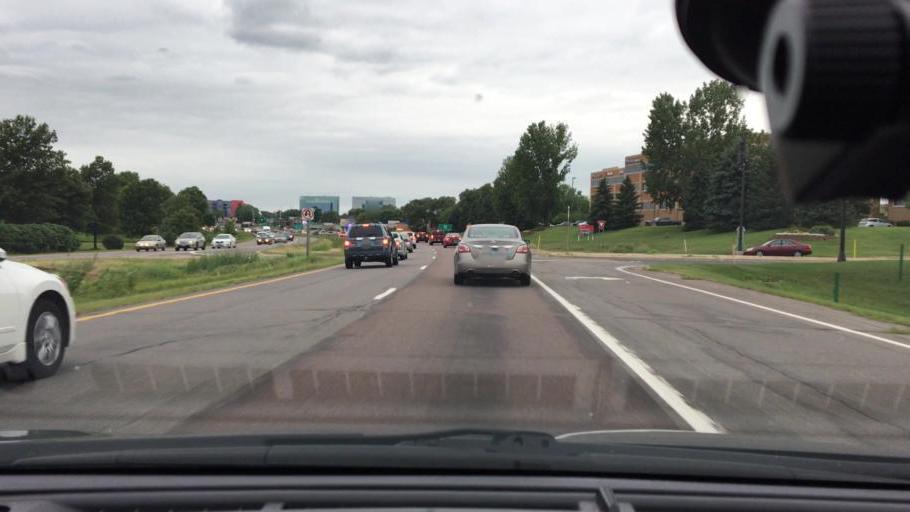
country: US
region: Minnesota
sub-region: Hennepin County
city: Golden Valley
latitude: 44.9848
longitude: -93.3848
